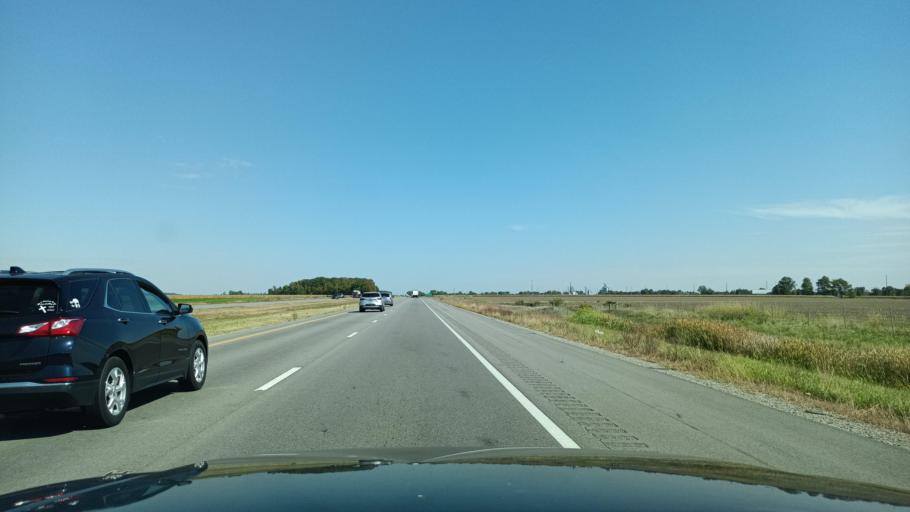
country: US
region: Ohio
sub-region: Henry County
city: Napoleon
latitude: 41.3492
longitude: -84.2438
